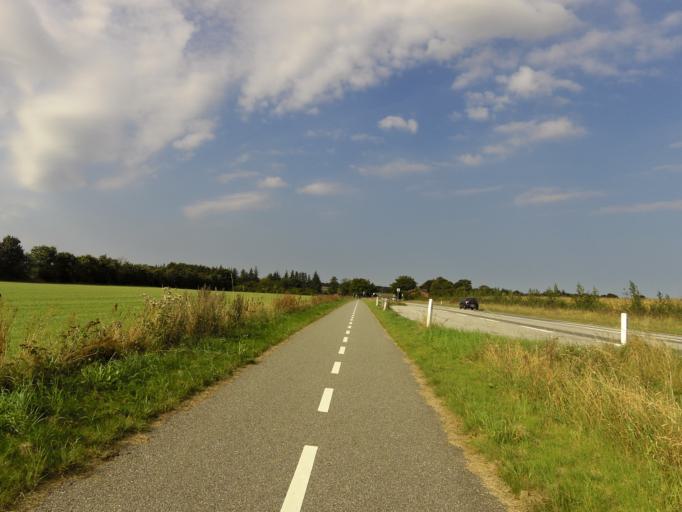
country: DK
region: South Denmark
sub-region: Vejen Kommune
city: Vejen
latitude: 55.4400
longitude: 9.1380
